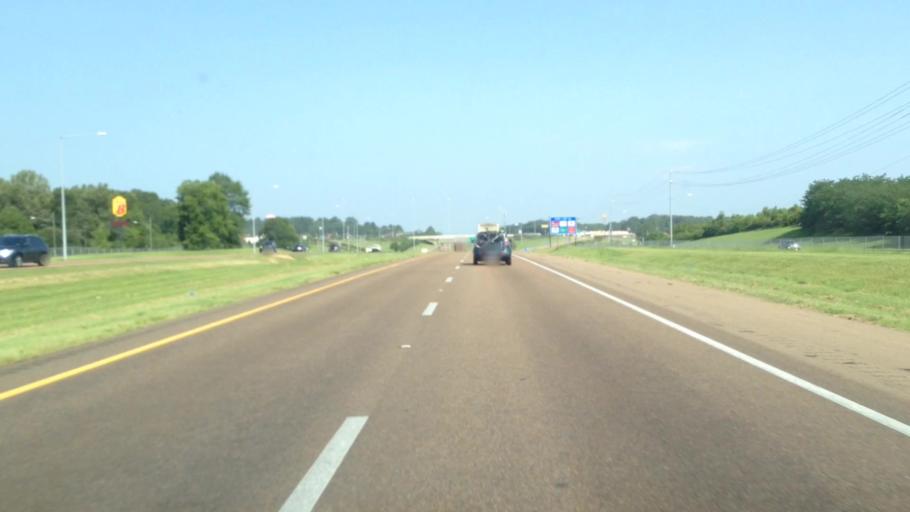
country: US
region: Mississippi
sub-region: Hinds County
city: Clinton
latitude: 32.3217
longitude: -90.3169
